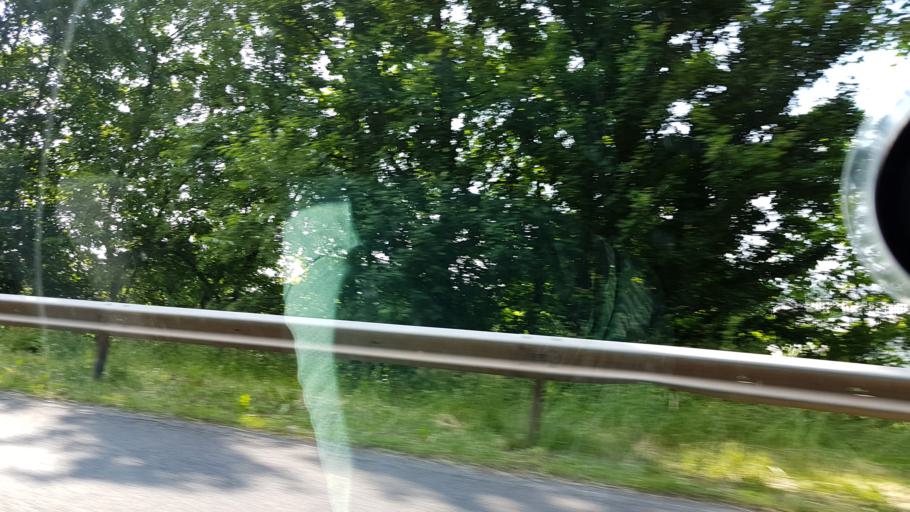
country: DE
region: Rheinland-Pfalz
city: Baumholder
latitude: 49.6107
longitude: 7.3305
